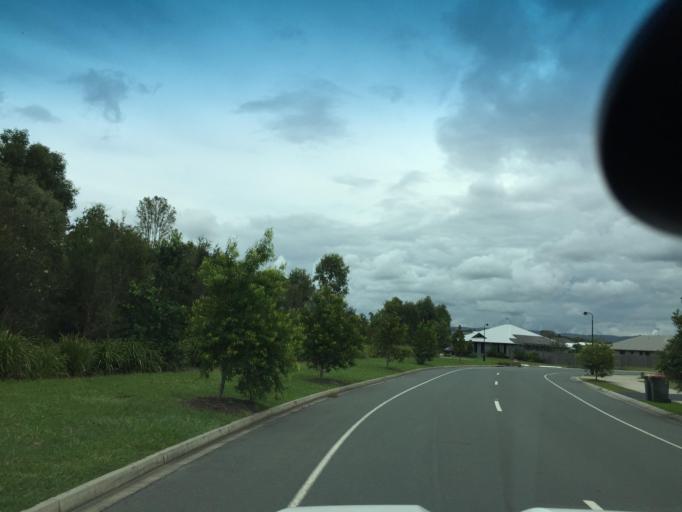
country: AU
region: Queensland
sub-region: Moreton Bay
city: Caboolture
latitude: -27.0656
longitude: 152.9324
